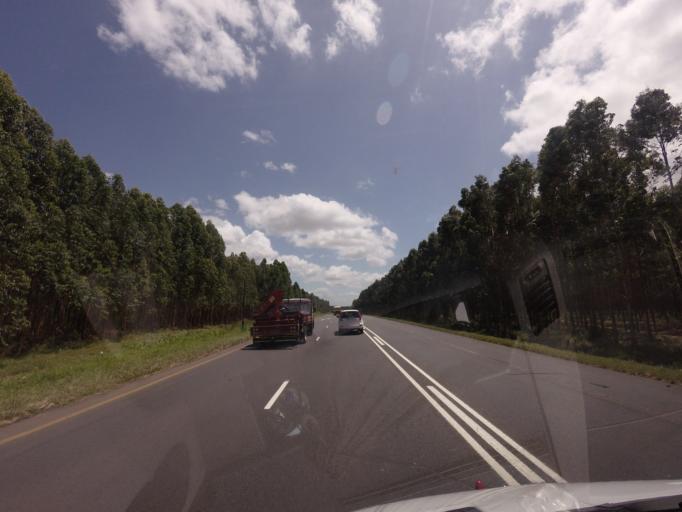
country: ZA
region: KwaZulu-Natal
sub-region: uThungulu District Municipality
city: KwaMbonambi
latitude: -28.5910
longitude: 32.0998
